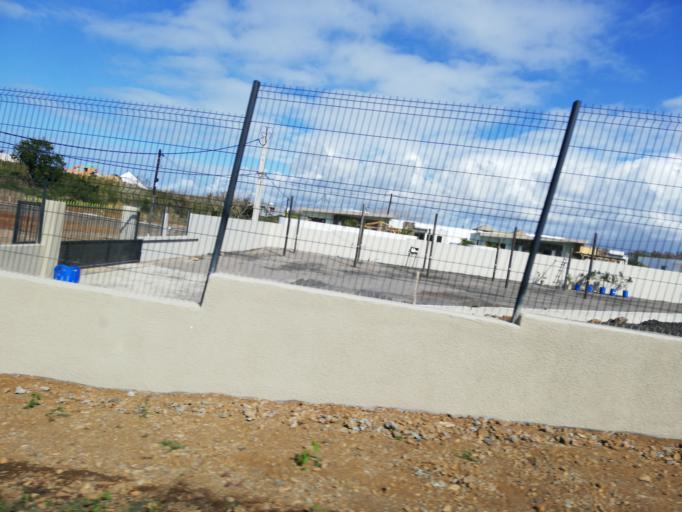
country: MU
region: Riviere du Rempart
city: Petit Raffray
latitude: -20.0039
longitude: 57.6040
